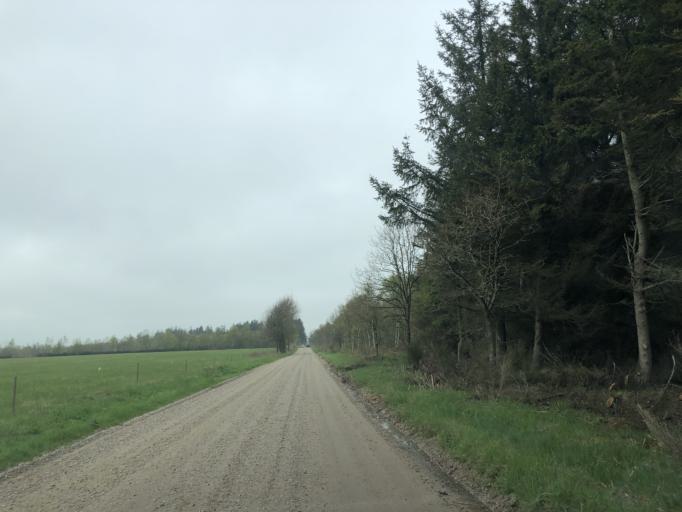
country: DK
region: Central Jutland
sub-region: Lemvig Kommune
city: Lemvig
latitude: 56.5023
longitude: 8.3300
